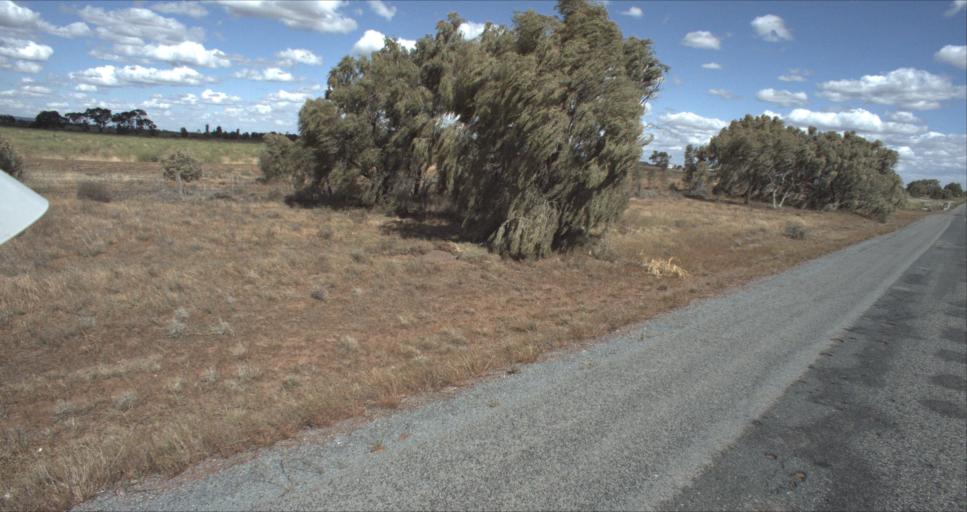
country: AU
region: New South Wales
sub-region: Leeton
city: Leeton
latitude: -34.4403
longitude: 146.2565
